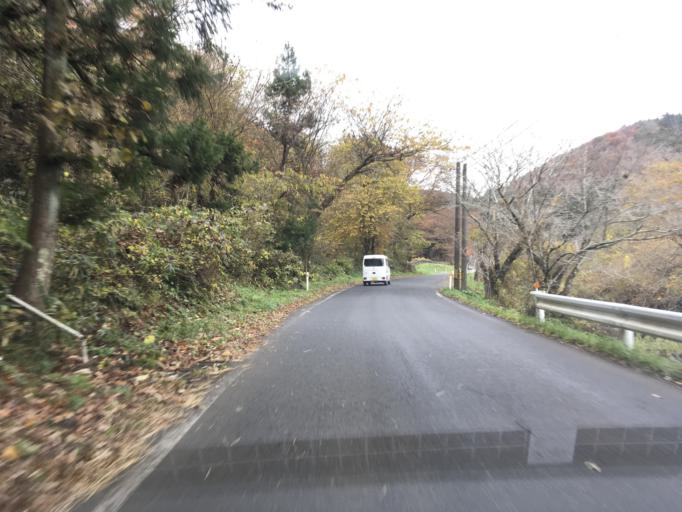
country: JP
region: Iwate
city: Mizusawa
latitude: 39.0960
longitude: 141.3436
